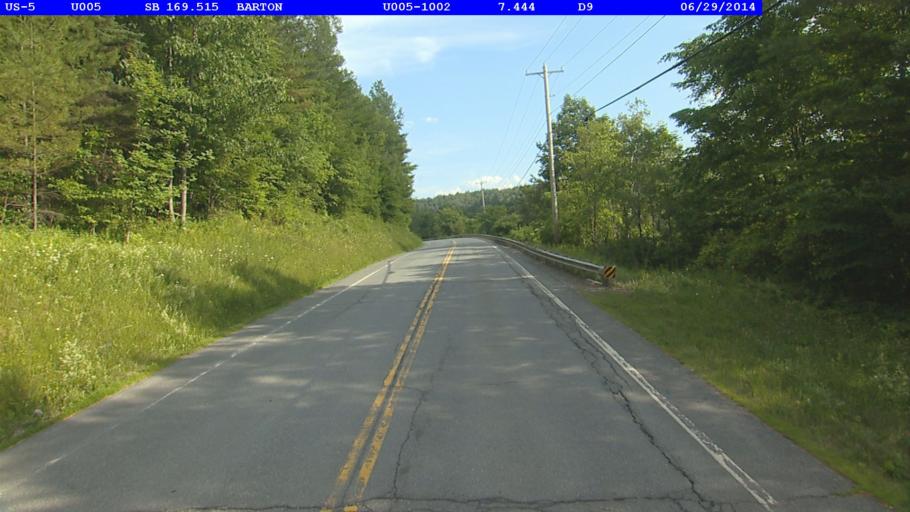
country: US
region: Vermont
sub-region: Orleans County
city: Newport
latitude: 44.7660
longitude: -72.2053
